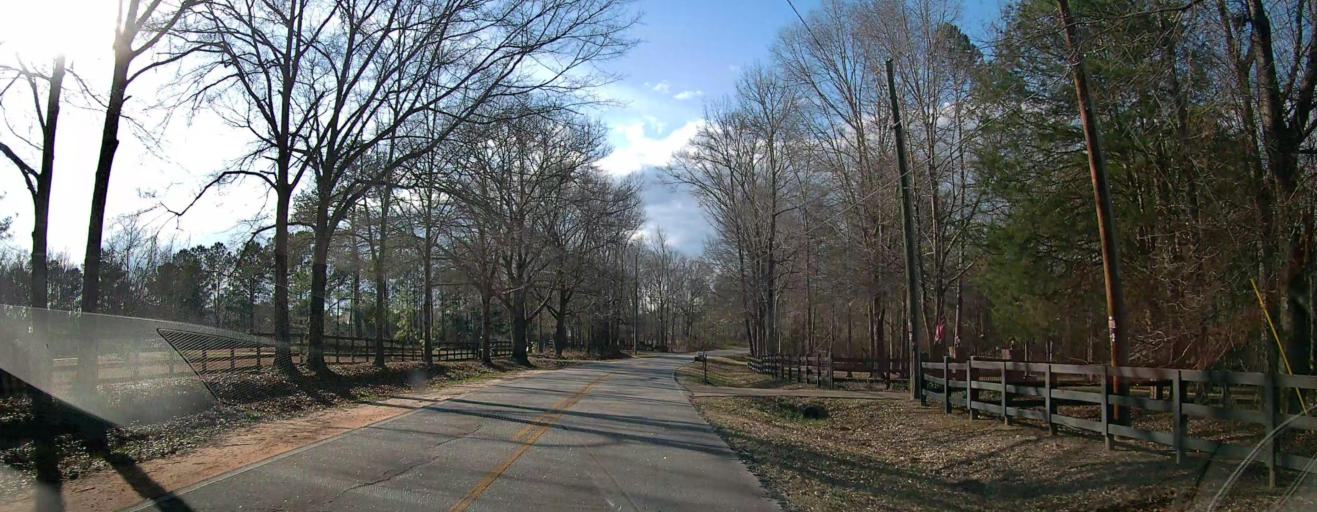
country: US
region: Georgia
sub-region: Harris County
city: Hamilton
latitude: 32.5660
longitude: -84.7995
